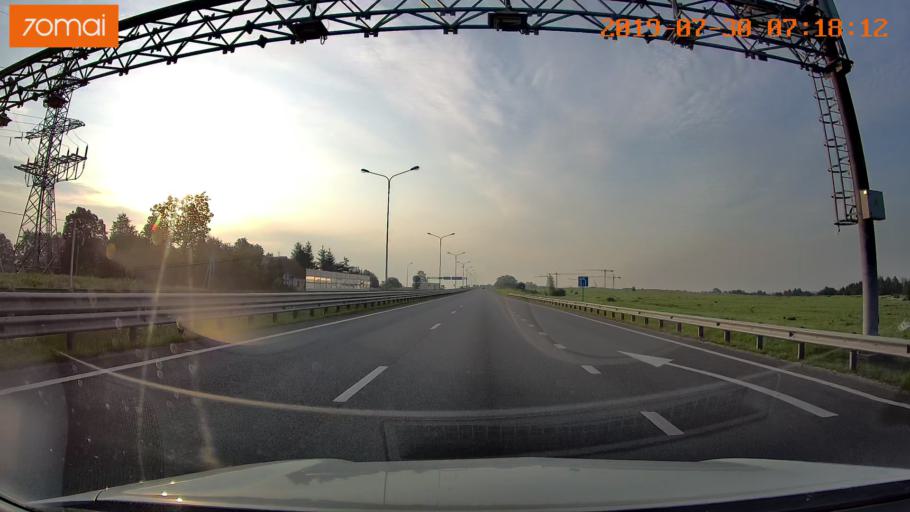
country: RU
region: Kaliningrad
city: Bol'shoe Isakovo
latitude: 54.7050
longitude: 20.6432
